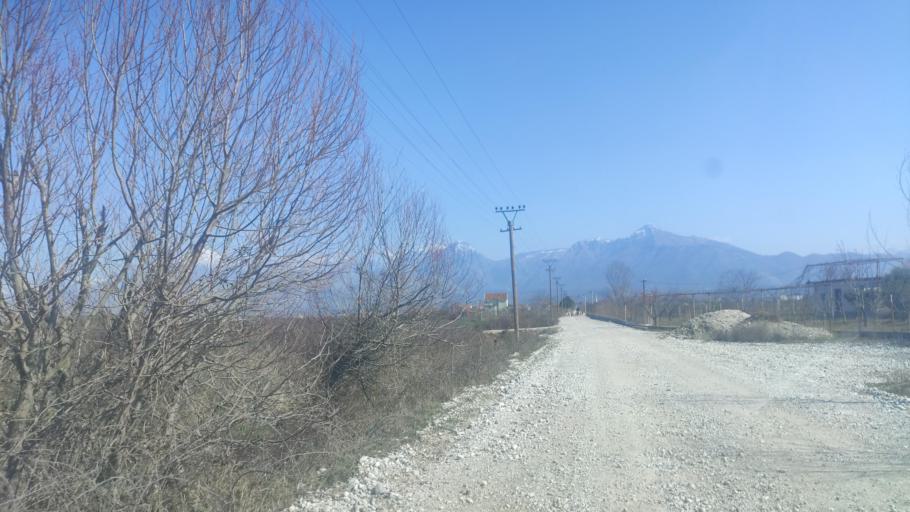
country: AL
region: Shkoder
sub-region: Rrethi i Malesia e Madhe
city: Grude-Fushe
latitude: 42.1582
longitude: 19.4473
